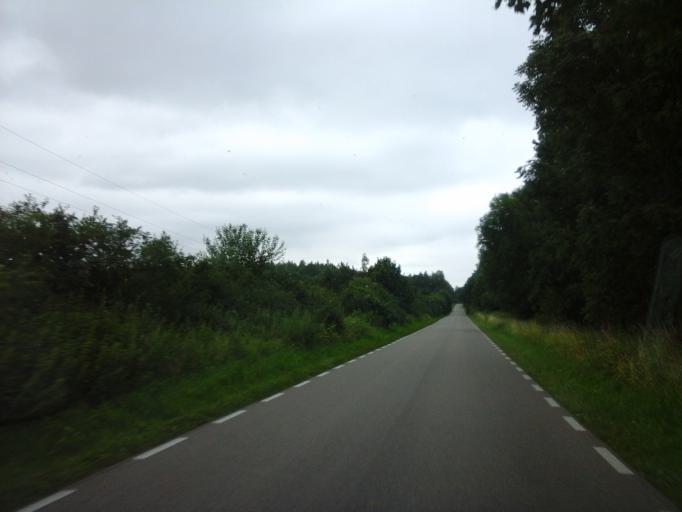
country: PL
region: West Pomeranian Voivodeship
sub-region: Powiat choszczenski
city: Pelczyce
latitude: 53.0928
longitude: 15.2699
